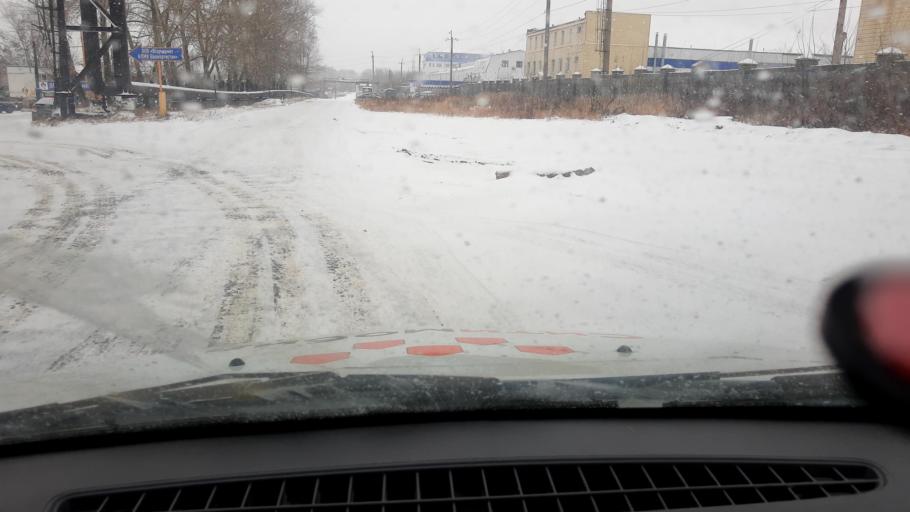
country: RU
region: Bashkortostan
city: Blagoveshchensk
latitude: 54.9113
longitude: 56.0777
